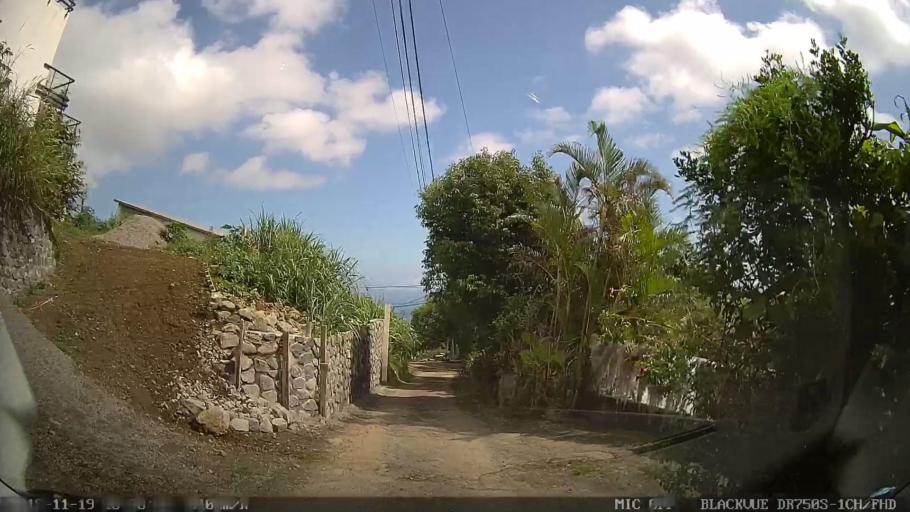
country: RE
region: Reunion
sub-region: Reunion
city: Sainte-Marie
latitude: -20.9413
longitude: 55.5295
